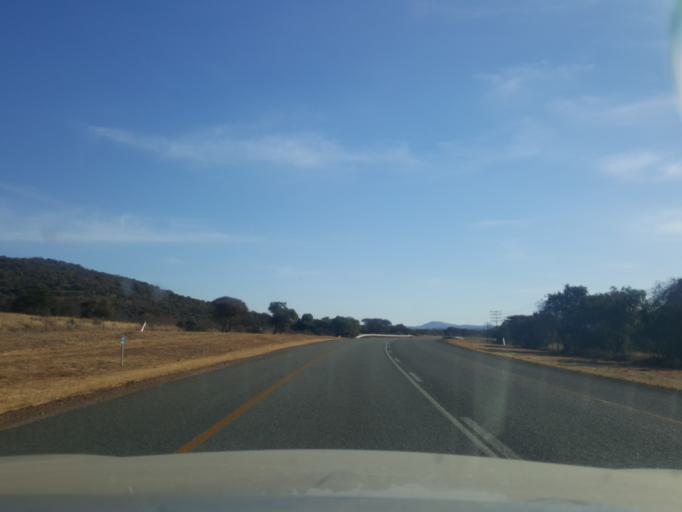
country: ZA
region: North-West
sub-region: Ngaka Modiri Molema District Municipality
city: Zeerust
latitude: -25.5412
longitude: 26.1200
